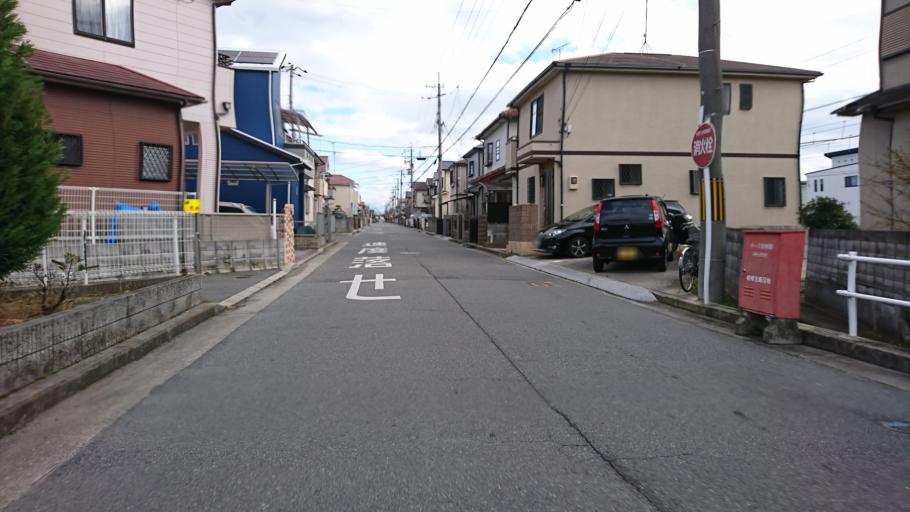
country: JP
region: Hyogo
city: Kakogawacho-honmachi
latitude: 34.7830
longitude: 134.8174
